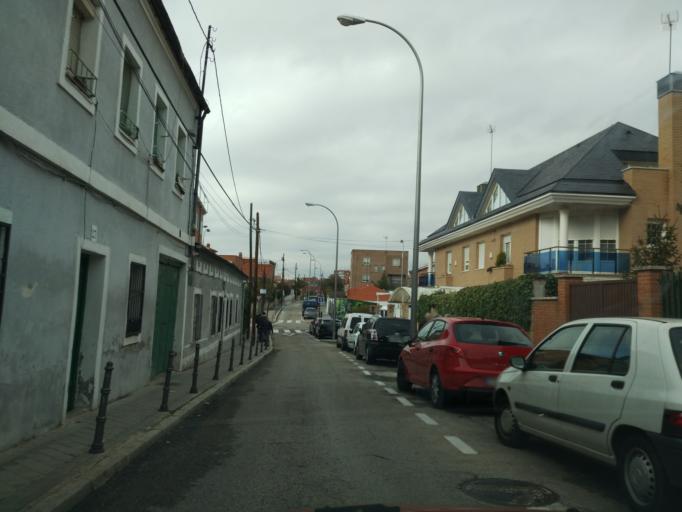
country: ES
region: Madrid
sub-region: Provincia de Madrid
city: Ciudad Lineal
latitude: 40.4648
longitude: -3.6500
